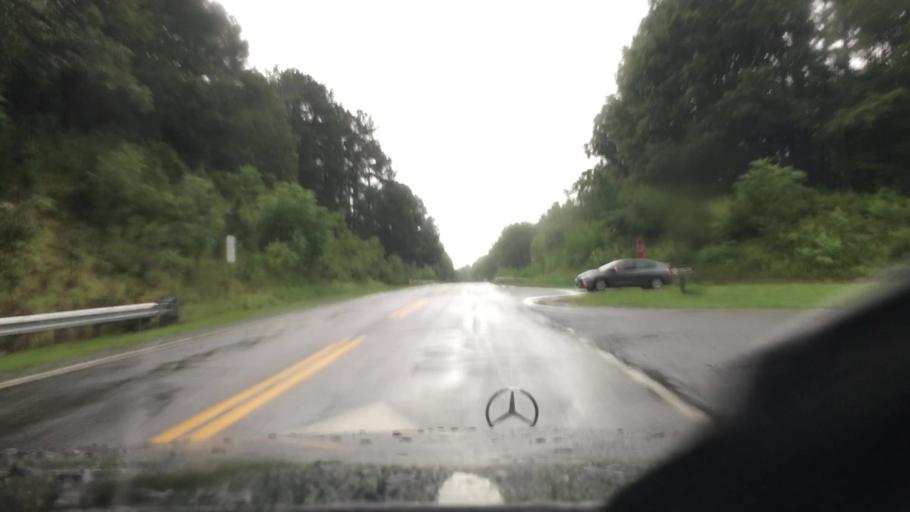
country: US
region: Virginia
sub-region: Campbell County
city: Altavista
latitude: 37.1375
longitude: -79.2917
